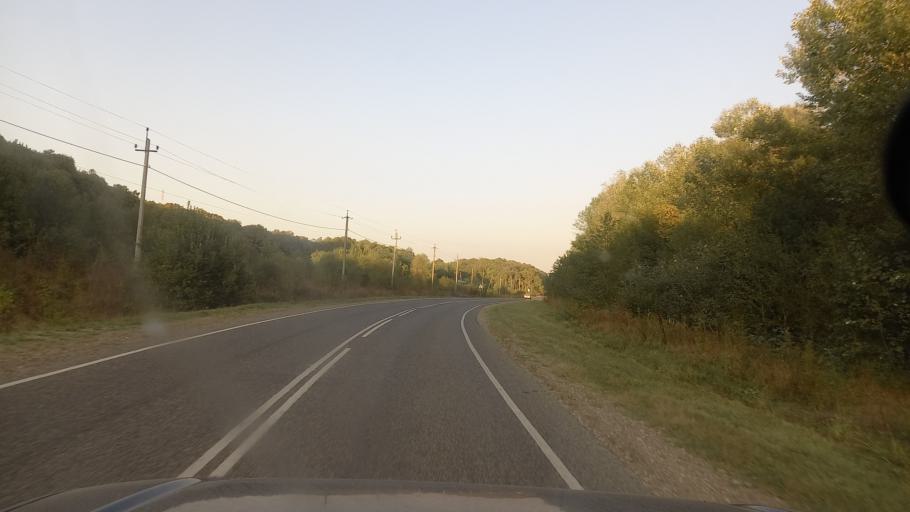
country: RU
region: Krasnodarskiy
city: Smolenskaya
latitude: 44.7466
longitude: 38.7535
